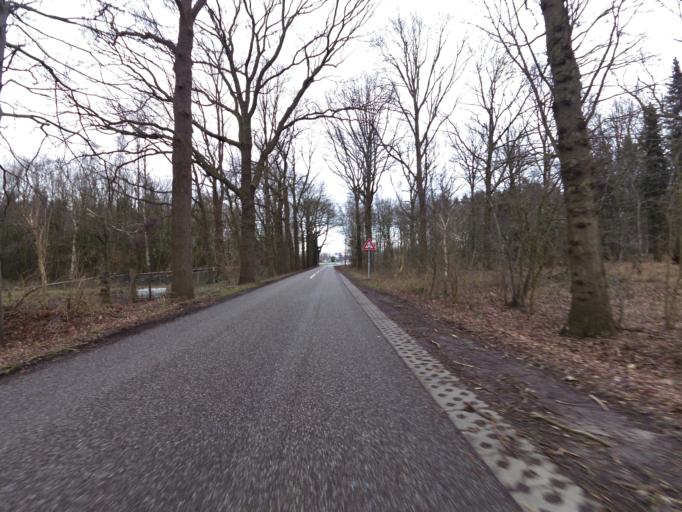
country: NL
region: Gelderland
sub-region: Oude IJsselstreek
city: Wisch
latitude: 51.9252
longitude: 6.3854
